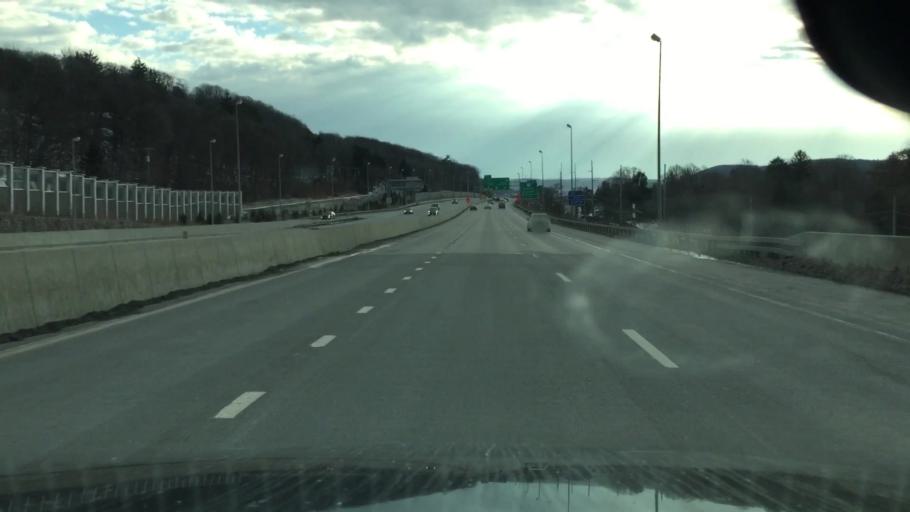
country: US
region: New York
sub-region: Broome County
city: Binghamton
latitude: 42.1137
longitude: -75.9273
